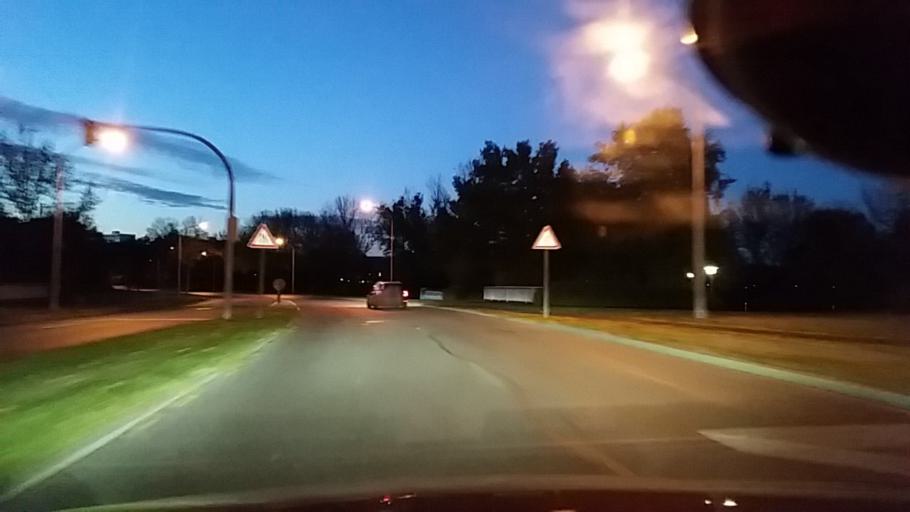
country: DE
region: Lower Saxony
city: Wolfsburg
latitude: 52.4441
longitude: 10.8062
